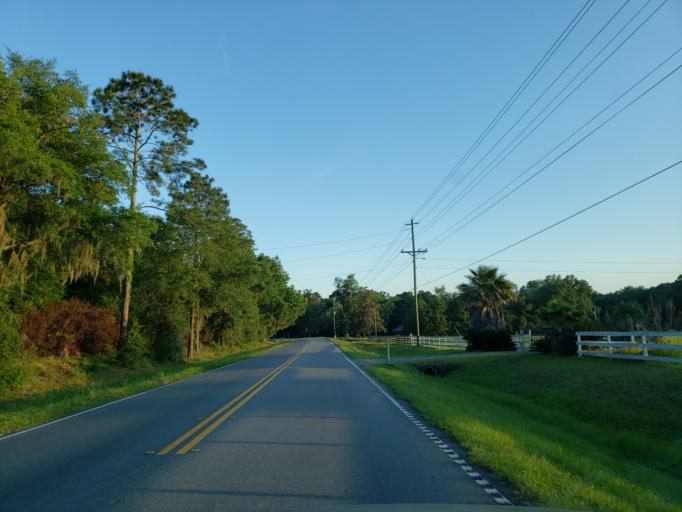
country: US
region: Georgia
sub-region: Lowndes County
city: Valdosta
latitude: 30.6878
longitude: -83.2396
